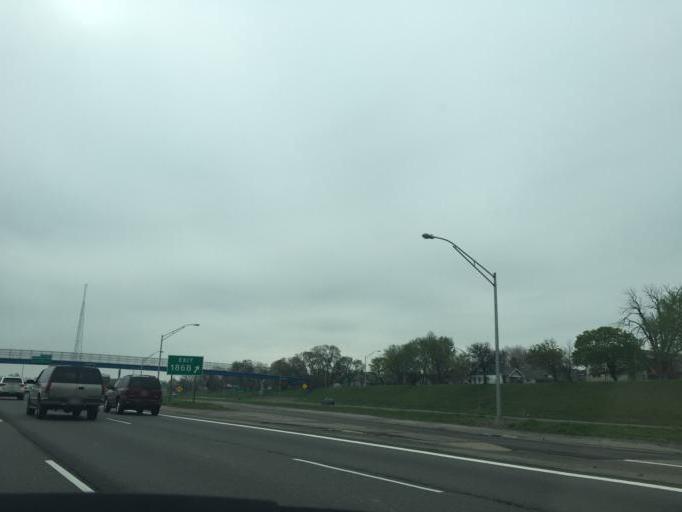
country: US
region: Michigan
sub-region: Wayne County
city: Highland Park
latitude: 42.3853
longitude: -83.1570
